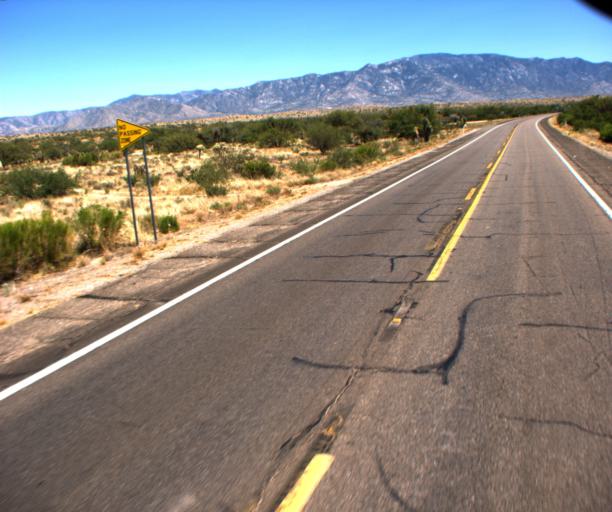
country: US
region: Arizona
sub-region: Pima County
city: Catalina
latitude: 32.5622
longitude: -110.9383
